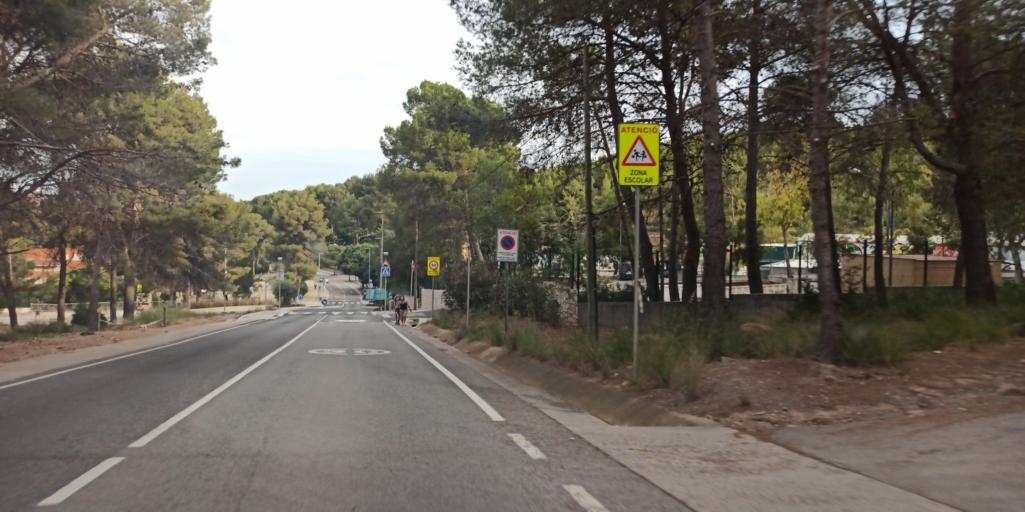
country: ES
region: Catalonia
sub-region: Provincia de Barcelona
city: Castelldefels
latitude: 41.2896
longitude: 1.9715
